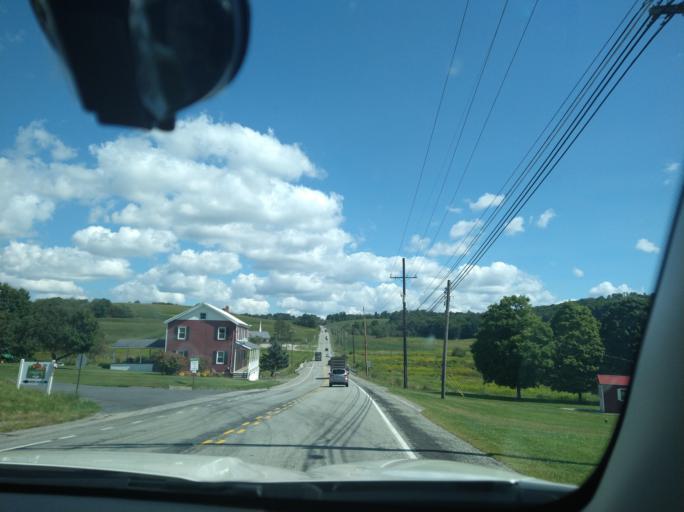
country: US
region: Pennsylvania
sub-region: Somerset County
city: Milford
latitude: 40.0222
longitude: -79.1862
